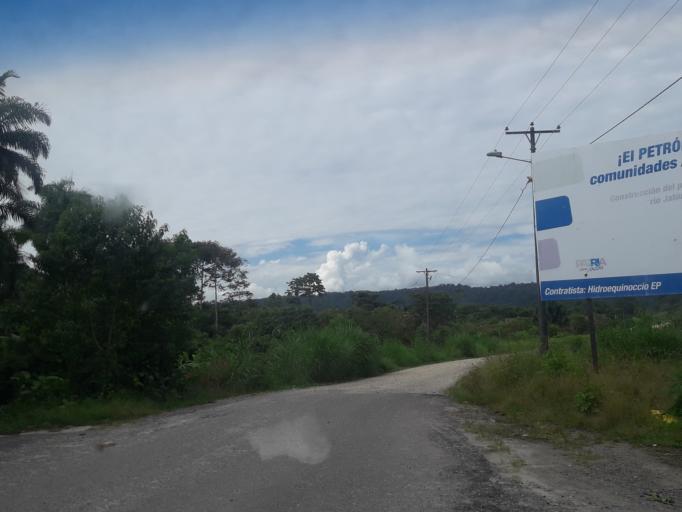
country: EC
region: Napo
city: Tena
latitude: -1.0687
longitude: -77.9072
